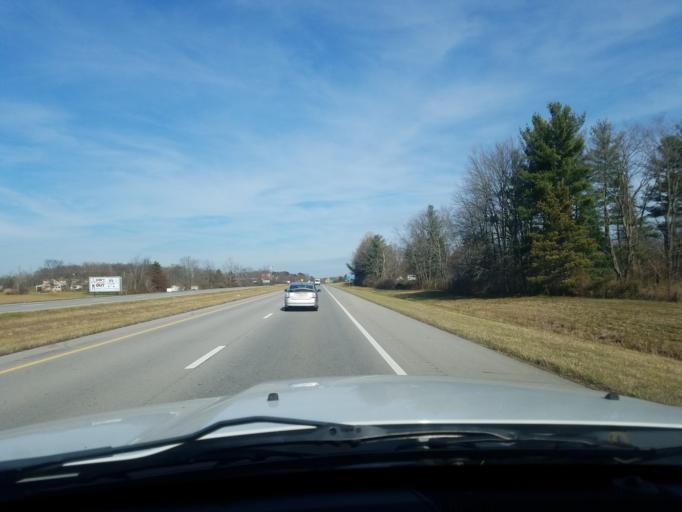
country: US
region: Ohio
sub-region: Athens County
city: Athens
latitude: 39.2296
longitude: -82.1972
